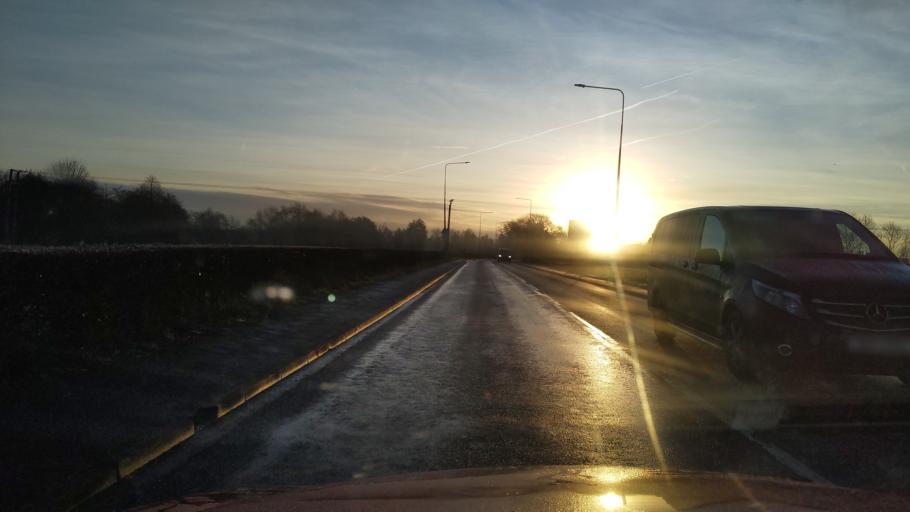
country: GB
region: England
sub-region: Lancashire
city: Coppull
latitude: 53.6290
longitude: -2.6849
